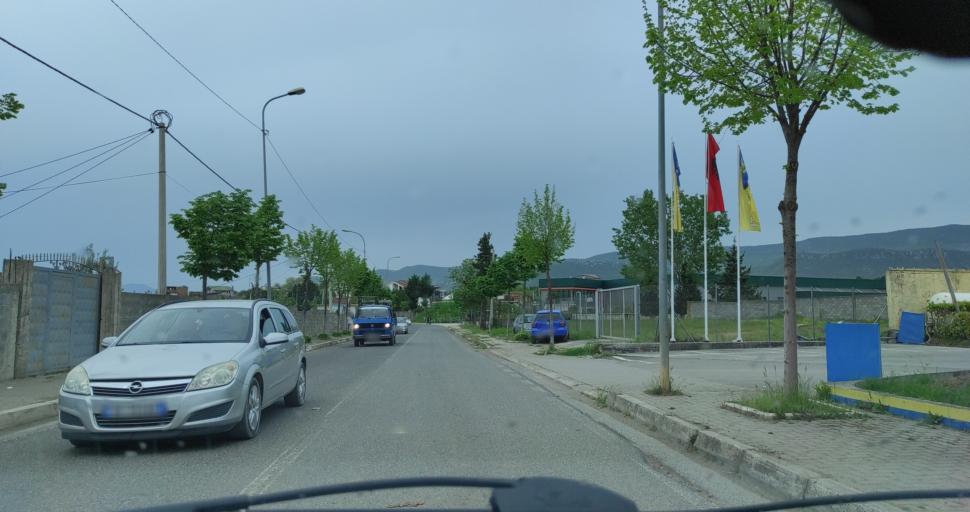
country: AL
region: Lezhe
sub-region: Rrethi i Kurbinit
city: Mamurras
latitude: 41.5830
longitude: 19.6925
